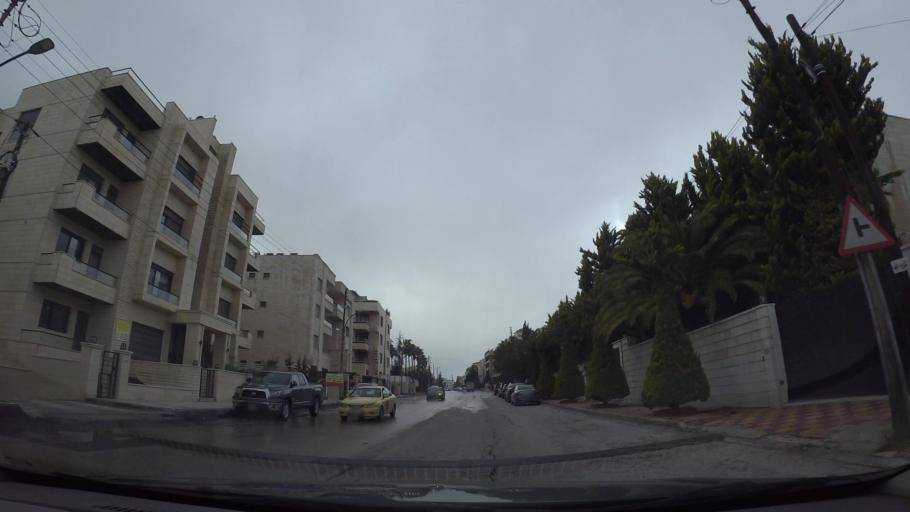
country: JO
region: Amman
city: Wadi as Sir
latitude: 31.9538
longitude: 35.8756
